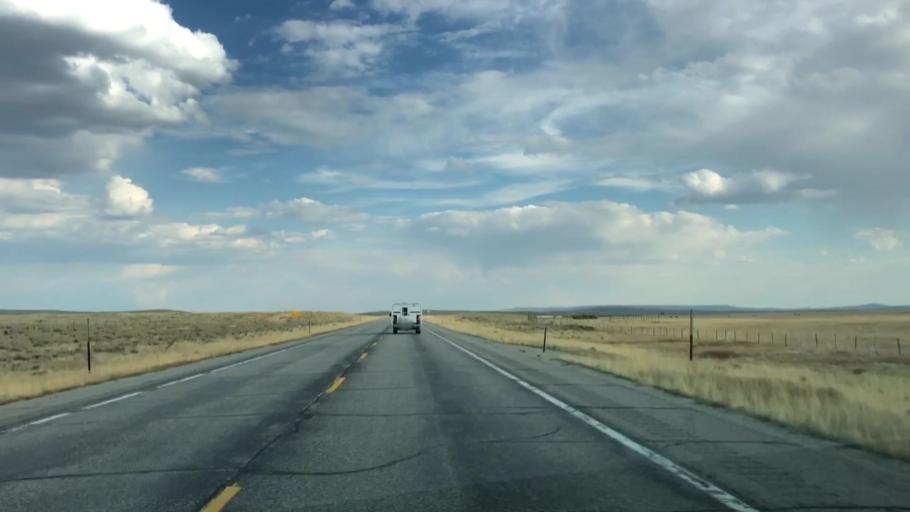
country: US
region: Wyoming
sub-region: Sublette County
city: Pinedale
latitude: 43.0403
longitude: -110.1391
